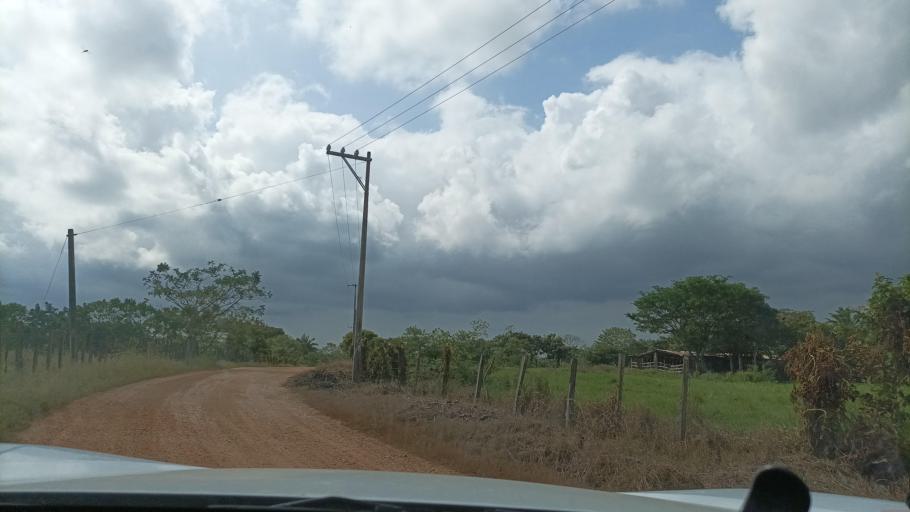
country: MX
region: Veracruz
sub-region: Chinameca
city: Chacalapa
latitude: 18.0841
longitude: -94.6737
